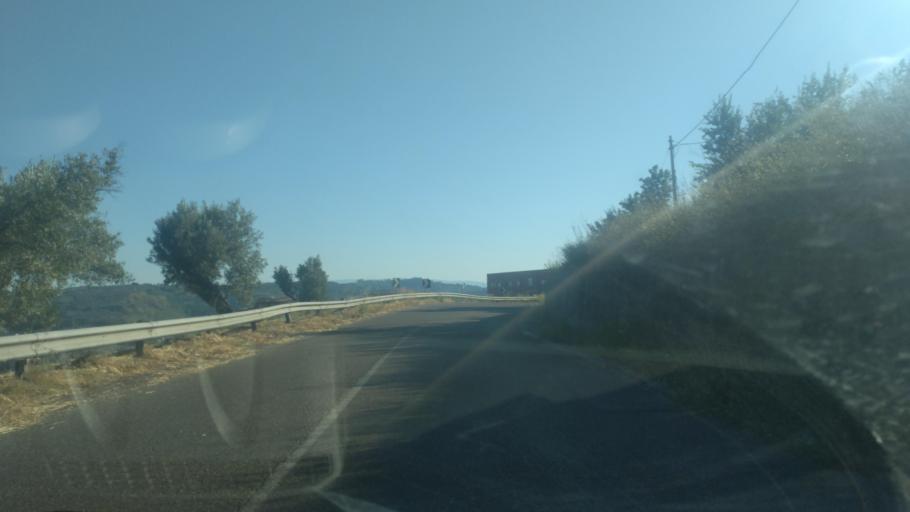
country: IT
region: Calabria
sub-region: Provincia di Catanzaro
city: Squillace
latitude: 38.7793
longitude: 16.5076
